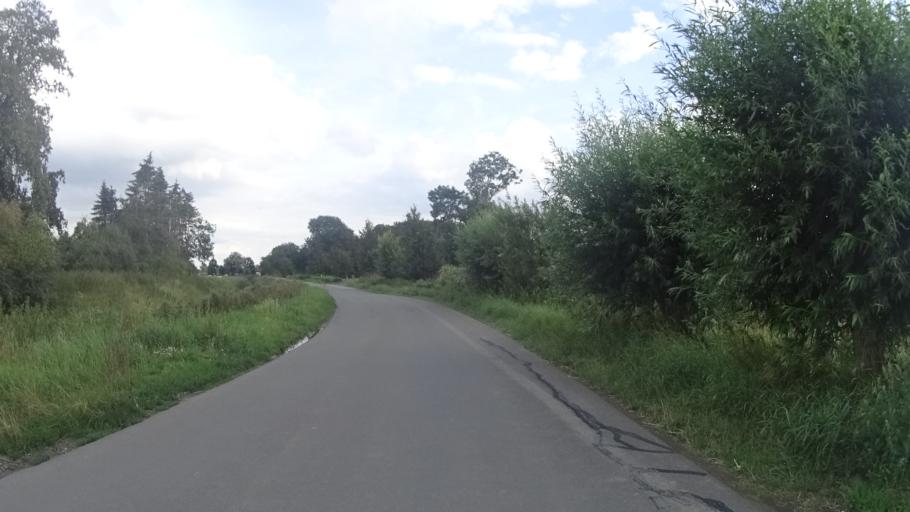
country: DE
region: Schleswig-Holstein
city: Herzhorn
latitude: 53.7747
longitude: 9.4854
